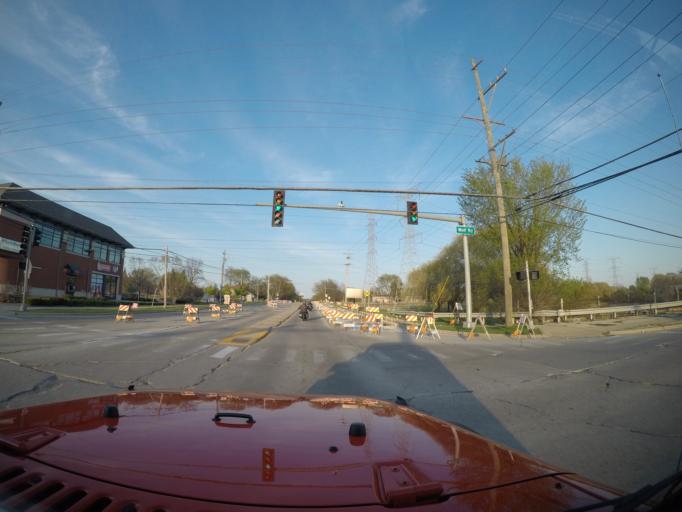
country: US
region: Illinois
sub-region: Cook County
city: Prospect Heights
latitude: 42.0879
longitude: -87.9077
